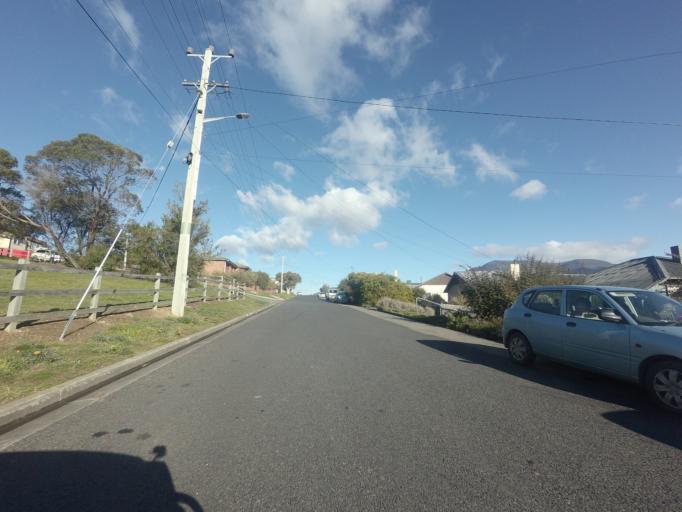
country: AU
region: Tasmania
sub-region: Glenorchy
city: Lutana
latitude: -42.8366
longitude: 147.3076
